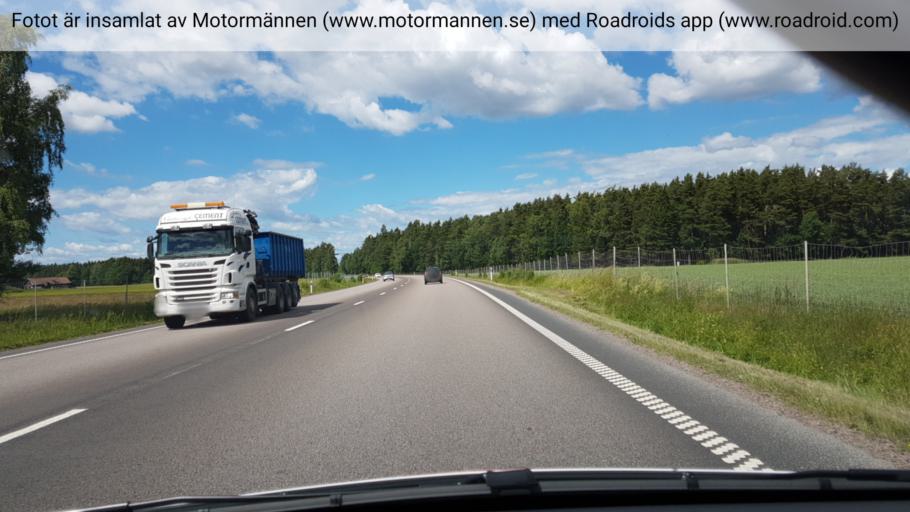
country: SE
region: Vaestra Goetaland
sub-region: Lidkopings Kommun
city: Vinninga
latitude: 58.4536
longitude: 13.2387
